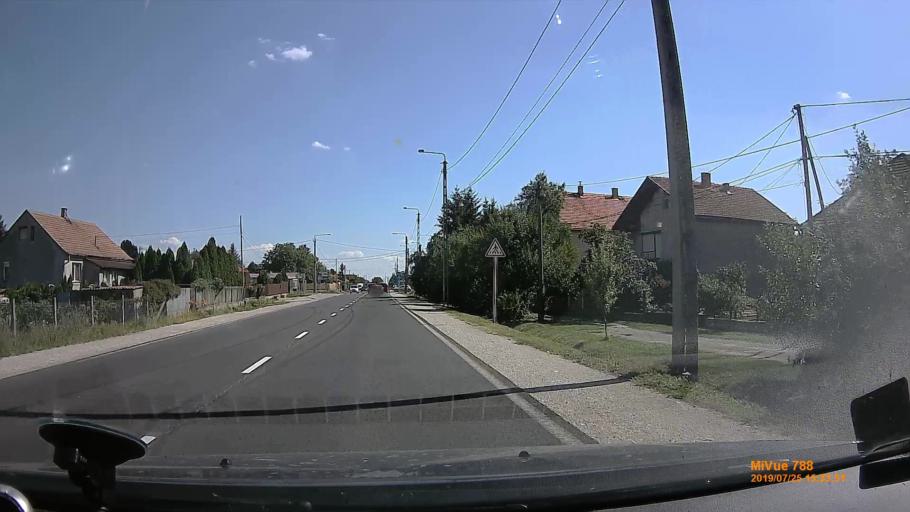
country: HU
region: Borsod-Abauj-Zemplen
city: Nyekladhaza
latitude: 47.9916
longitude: 20.8304
